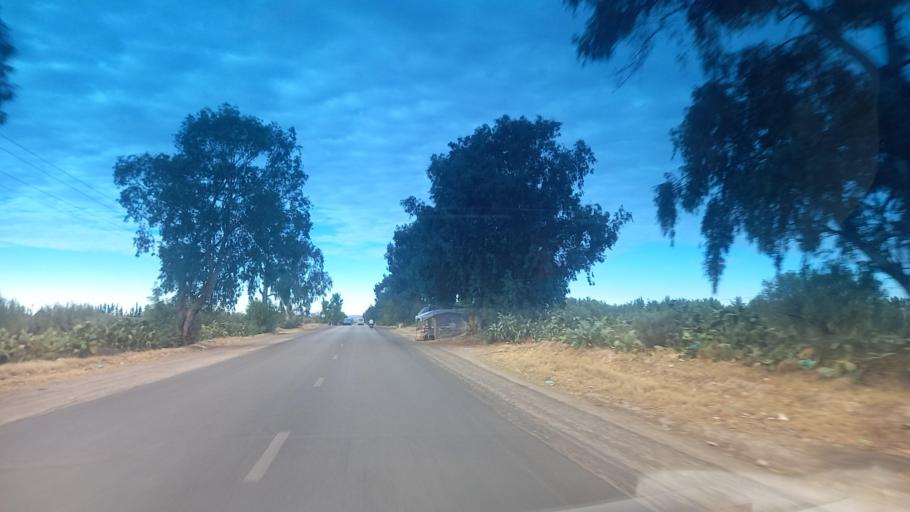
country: TN
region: Al Qasrayn
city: Sbiba
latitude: 35.2724
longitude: 9.0934
